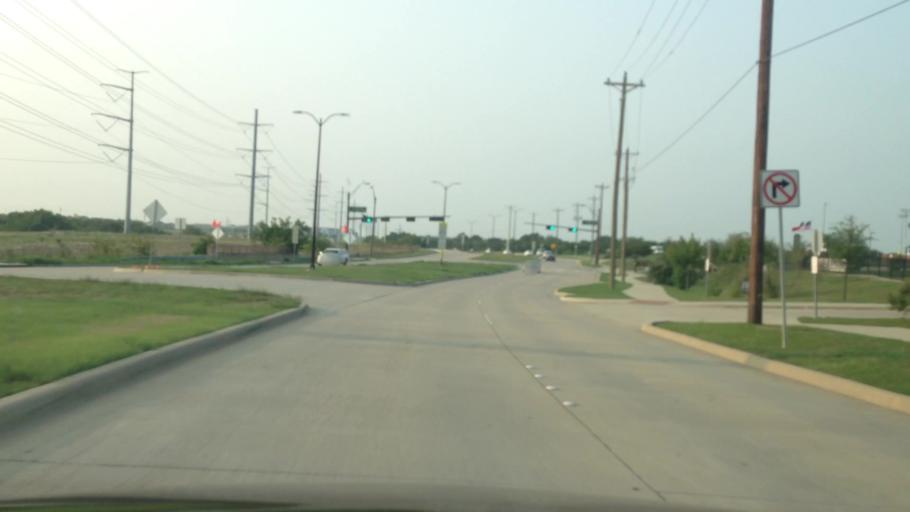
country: US
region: Texas
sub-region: Collin County
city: Frisco
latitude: 33.1268
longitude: -96.8479
